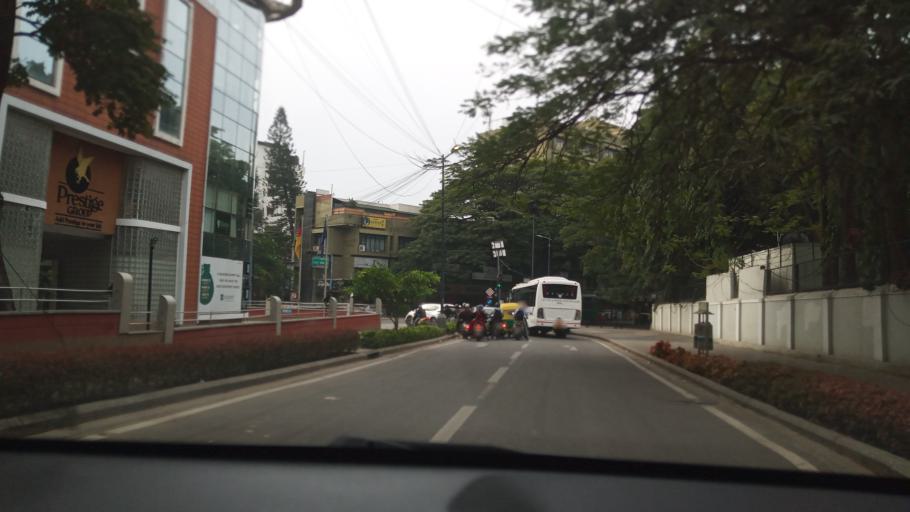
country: IN
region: Karnataka
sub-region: Bangalore Urban
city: Bangalore
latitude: 12.9686
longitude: 77.6003
